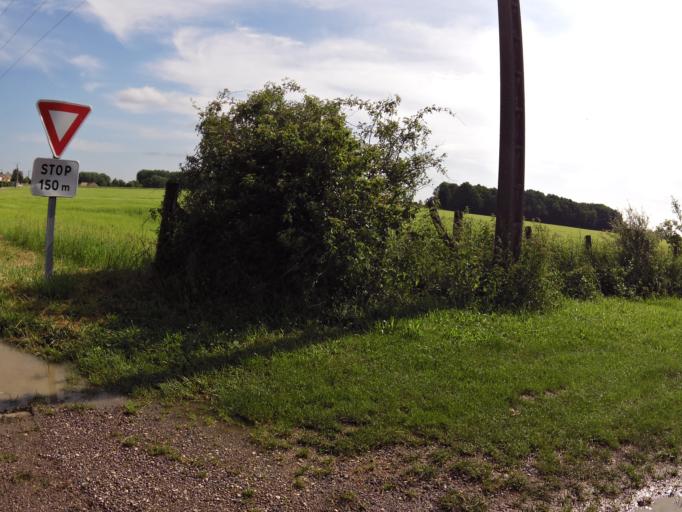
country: FR
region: Champagne-Ardenne
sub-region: Departement de l'Aube
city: Verrieres
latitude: 48.2664
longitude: 4.1795
